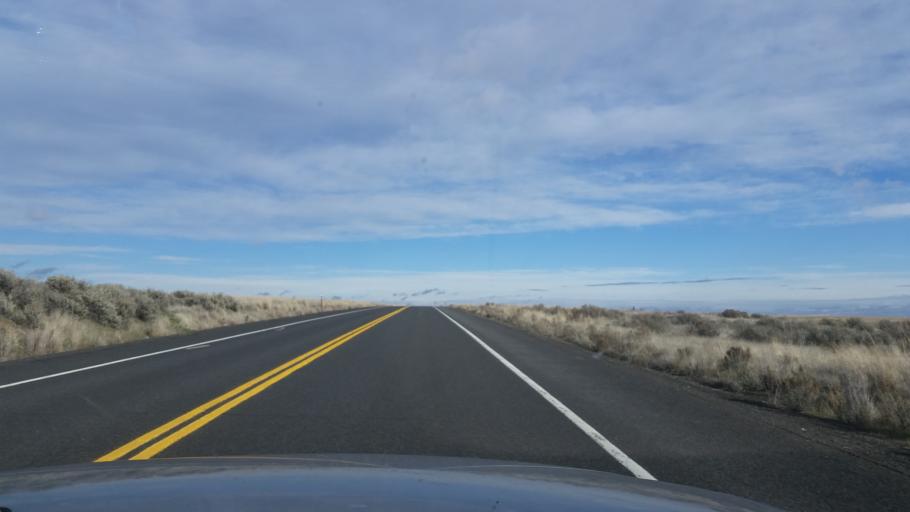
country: US
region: Washington
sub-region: Adams County
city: Ritzville
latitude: 47.3701
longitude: -118.4504
